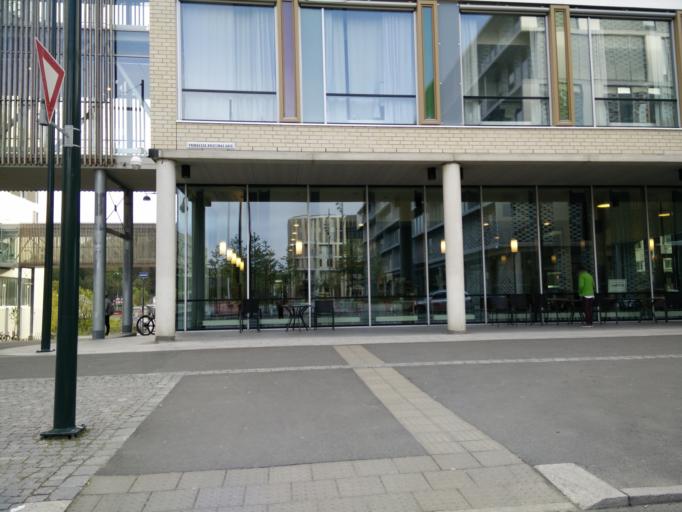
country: NO
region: Sor-Trondelag
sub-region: Trondheim
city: Trondheim
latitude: 63.4204
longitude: 10.3867
